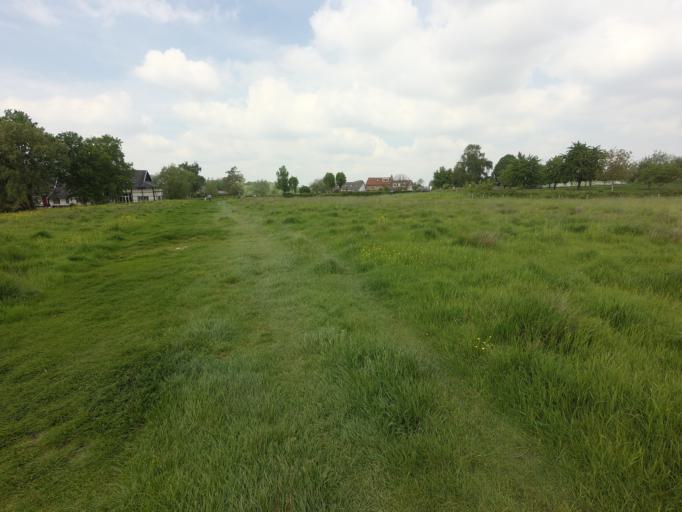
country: BE
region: Wallonia
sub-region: Province de Liege
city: Plombieres
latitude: 50.7843
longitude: 5.9216
